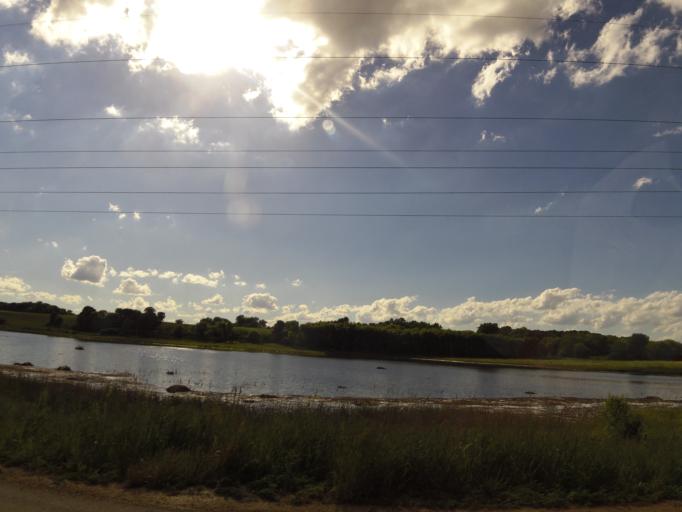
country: US
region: Minnesota
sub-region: Carver County
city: Waconia
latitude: 44.8714
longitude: -93.8132
